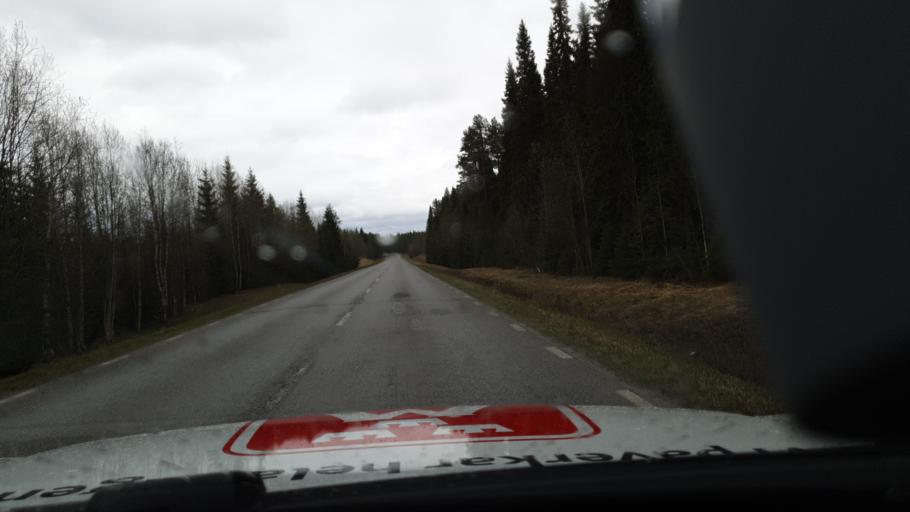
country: SE
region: Jaemtland
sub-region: Stroemsunds Kommun
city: Stroemsund
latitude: 63.6096
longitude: 15.2862
